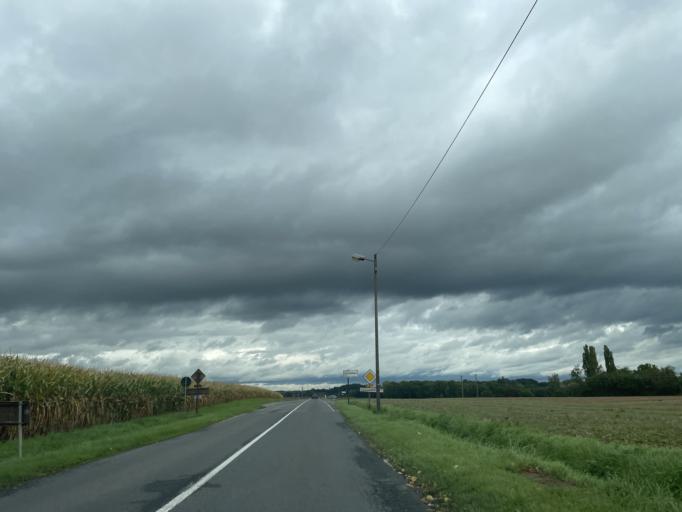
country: FR
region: Ile-de-France
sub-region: Departement de Seine-et-Marne
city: Coulommiers
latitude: 48.8284
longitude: 3.0873
